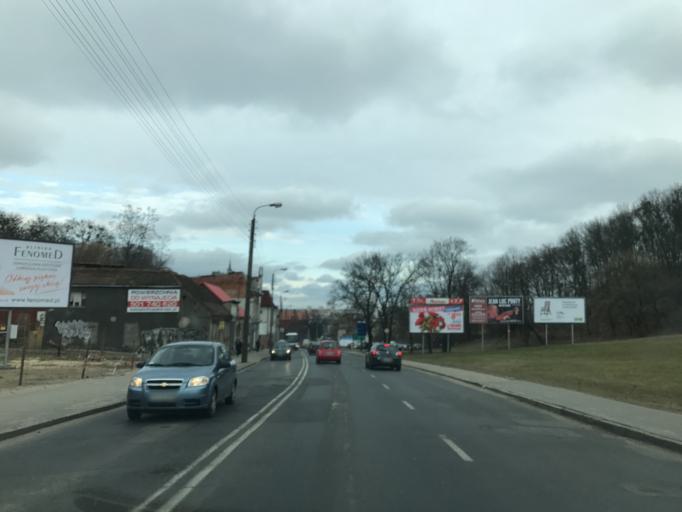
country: PL
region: Kujawsko-Pomorskie
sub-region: Bydgoszcz
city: Bydgoszcz
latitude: 53.1167
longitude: 18.0067
